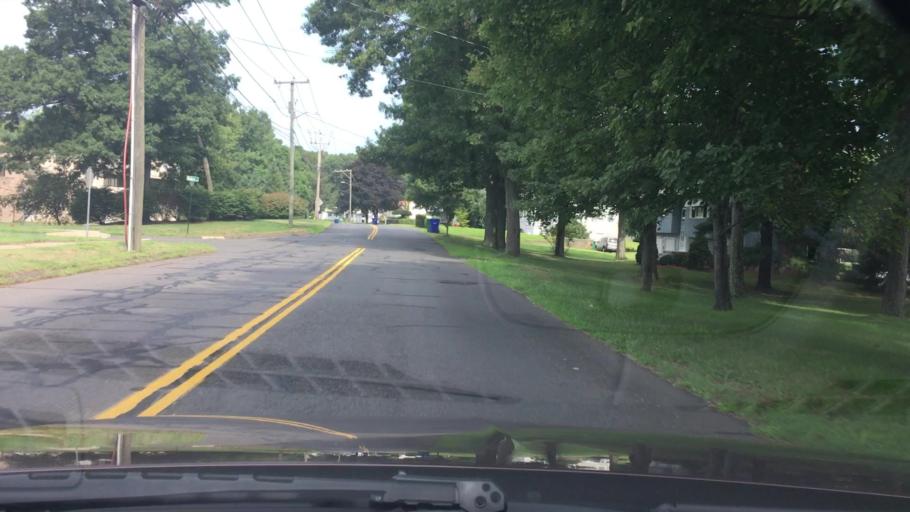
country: US
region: Connecticut
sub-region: Hartford County
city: South Windsor
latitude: 41.8274
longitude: -72.5894
